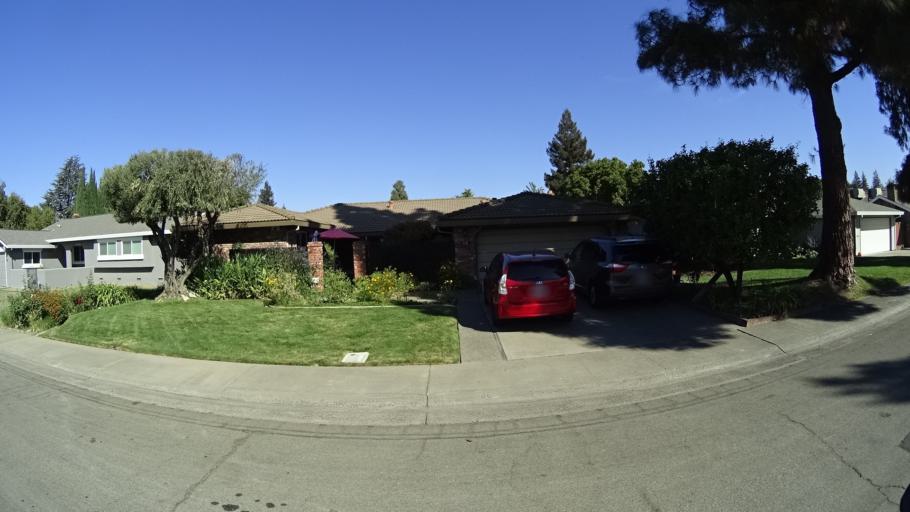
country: US
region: California
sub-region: Sacramento County
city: Parkway
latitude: 38.5036
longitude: -121.5223
